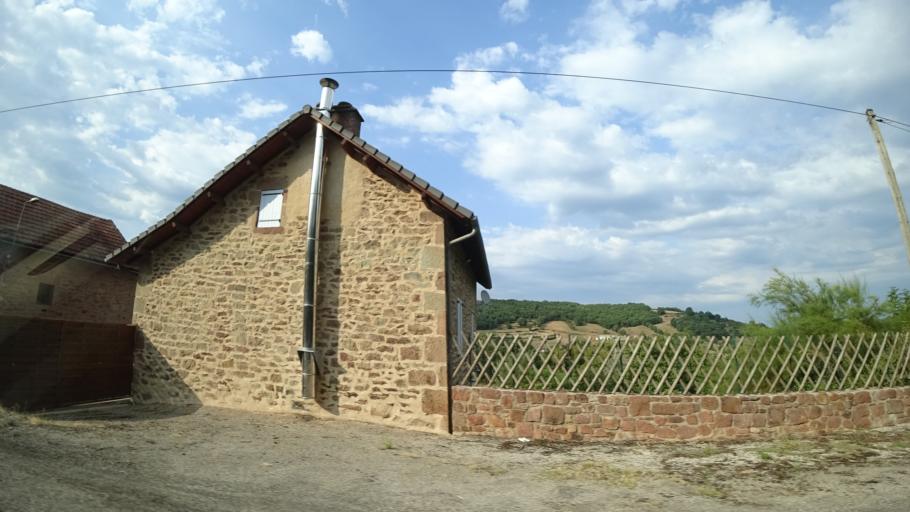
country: FR
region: Midi-Pyrenees
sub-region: Departement de l'Aveyron
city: Saint-Christophe-Vallon
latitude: 44.4995
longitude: 2.3741
